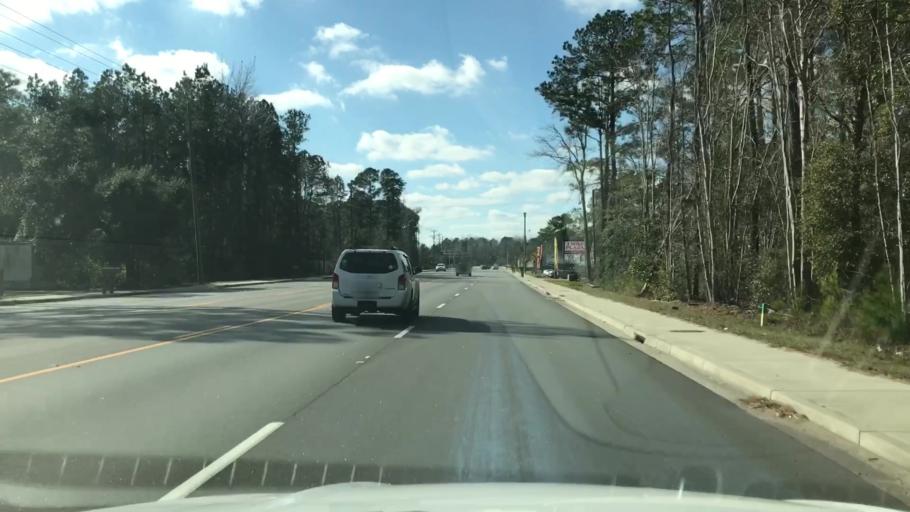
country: US
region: South Carolina
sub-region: Horry County
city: Socastee
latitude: 33.6425
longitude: -79.0290
